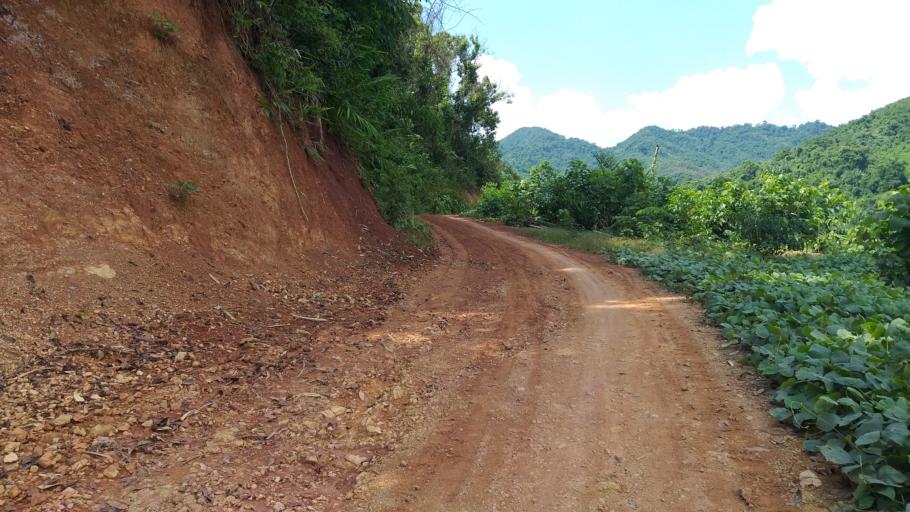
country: LA
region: Phongsali
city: Khoa
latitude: 21.3051
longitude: 102.5600
